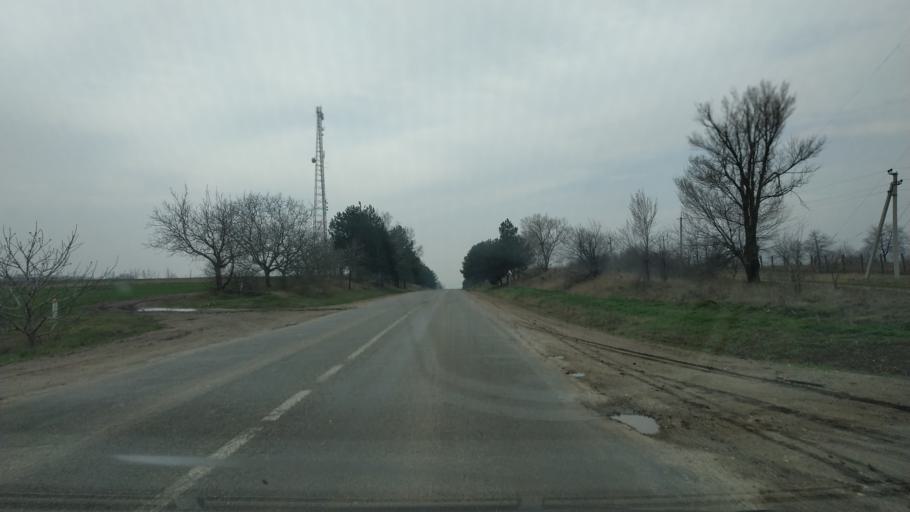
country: MD
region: Cahul
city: Cahul
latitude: 45.9339
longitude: 28.2789
